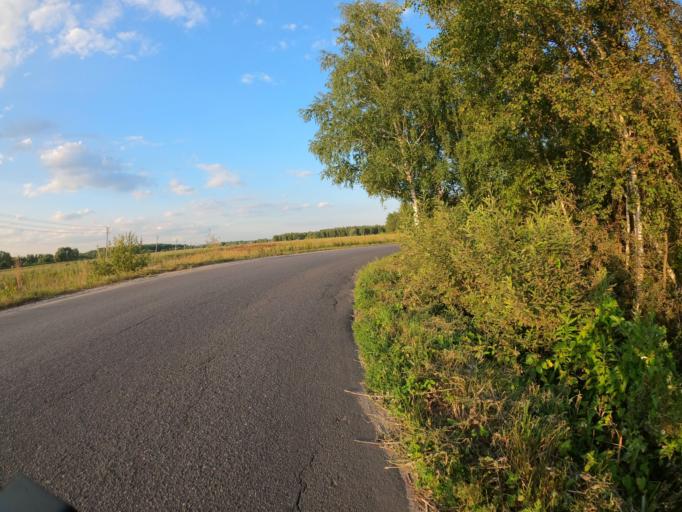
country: RU
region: Moskovskaya
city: Malyshevo
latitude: 55.5180
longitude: 38.2852
